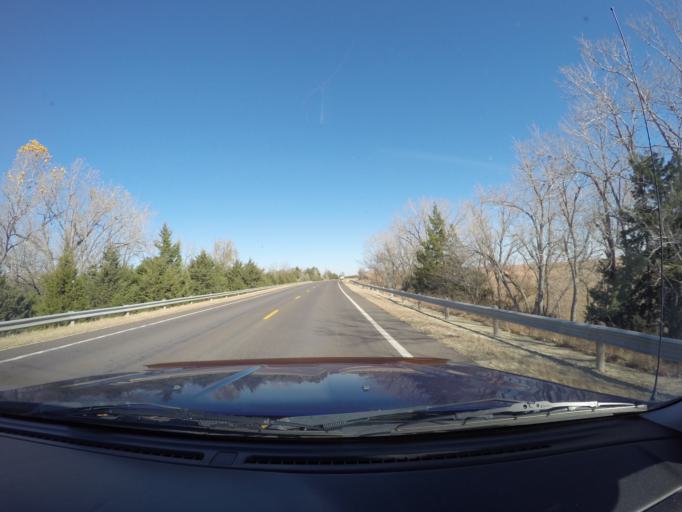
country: US
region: Kansas
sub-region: Marshall County
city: Blue Rapids
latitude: 39.4506
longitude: -96.7642
